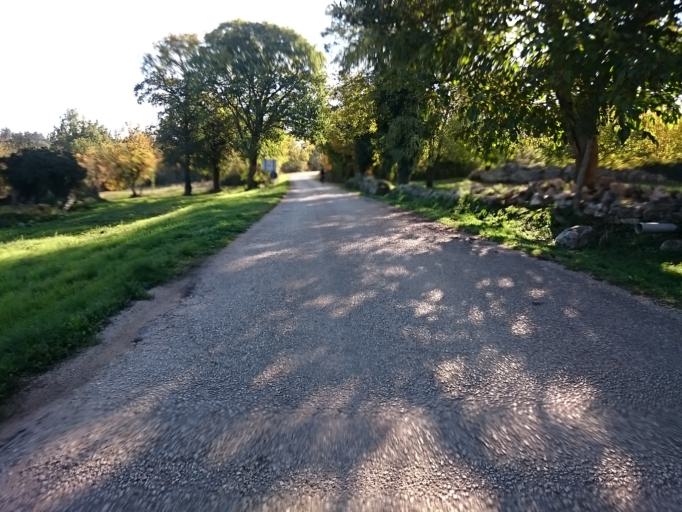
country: HR
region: Istarska
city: Buje
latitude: 45.3994
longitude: 13.7212
